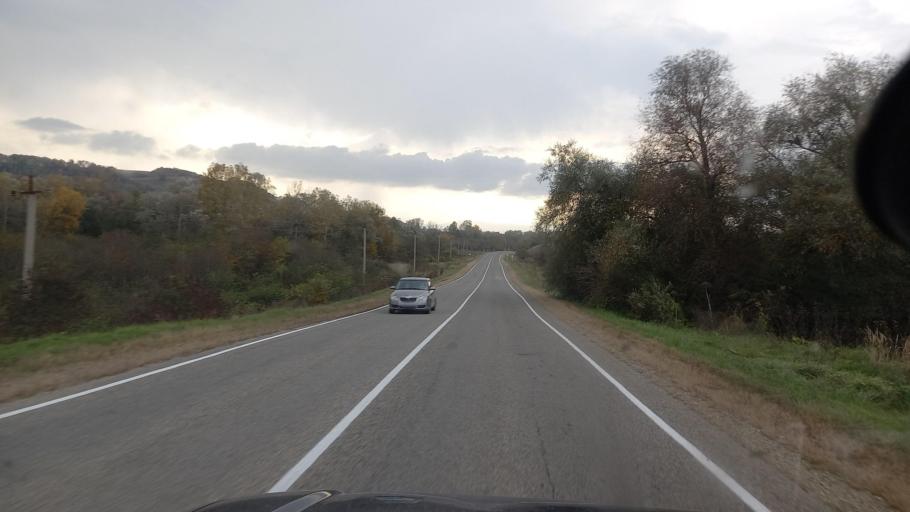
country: RU
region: Krasnodarskiy
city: Perepravnaya
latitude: 44.3745
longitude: 40.7335
